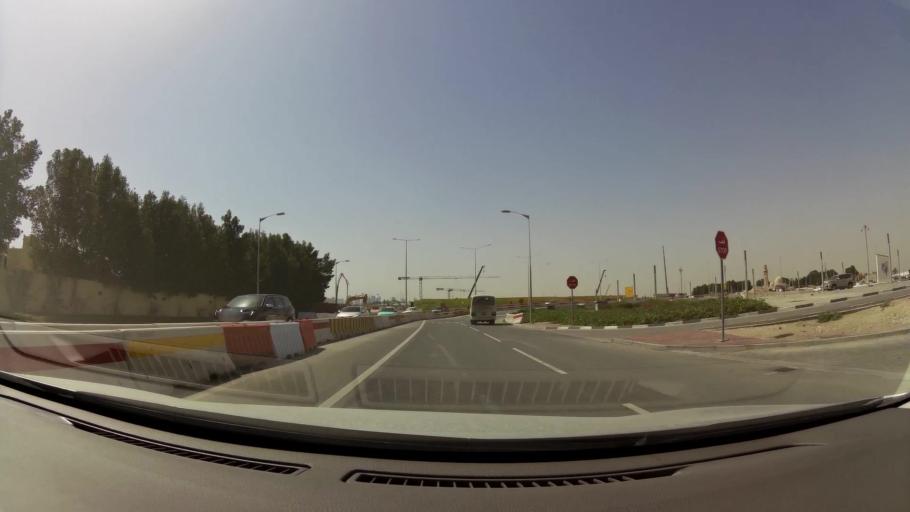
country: QA
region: Baladiyat ad Dawhah
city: Doha
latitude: 25.3748
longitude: 51.5255
